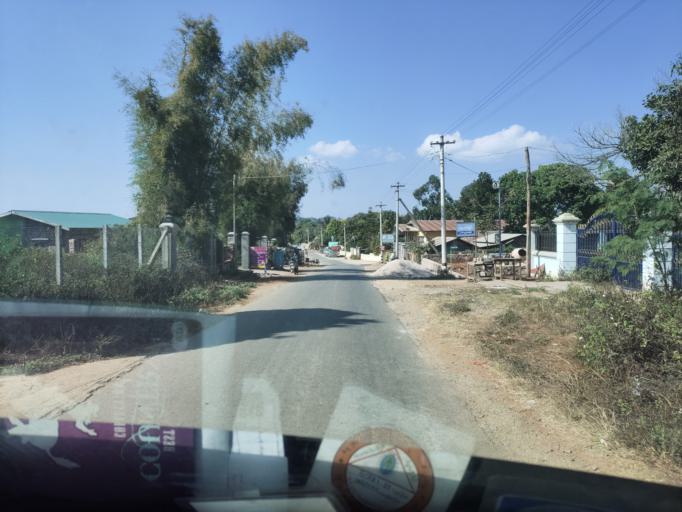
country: MM
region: Mandalay
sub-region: Pyin Oo Lwin District
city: Pyin Oo Lwin
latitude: 21.9527
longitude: 96.3953
